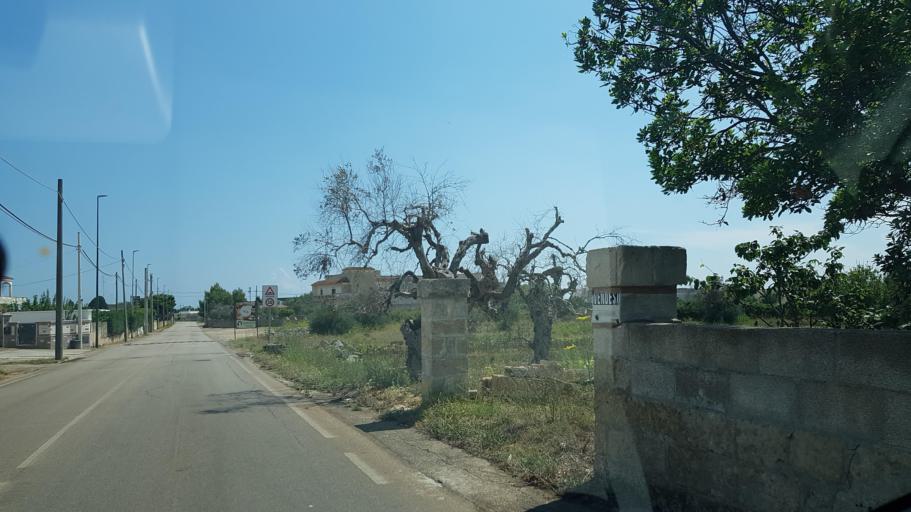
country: IT
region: Apulia
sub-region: Provincia di Lecce
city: Castrignano del Capo
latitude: 39.8282
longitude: 18.3524
